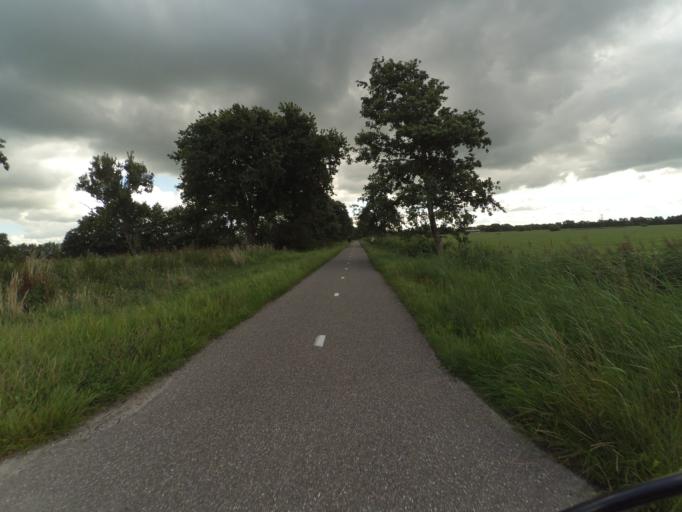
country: NL
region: Friesland
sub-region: Gemeente Tytsjerksteradiel
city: Hurdegaryp
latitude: 53.2068
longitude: 5.9527
